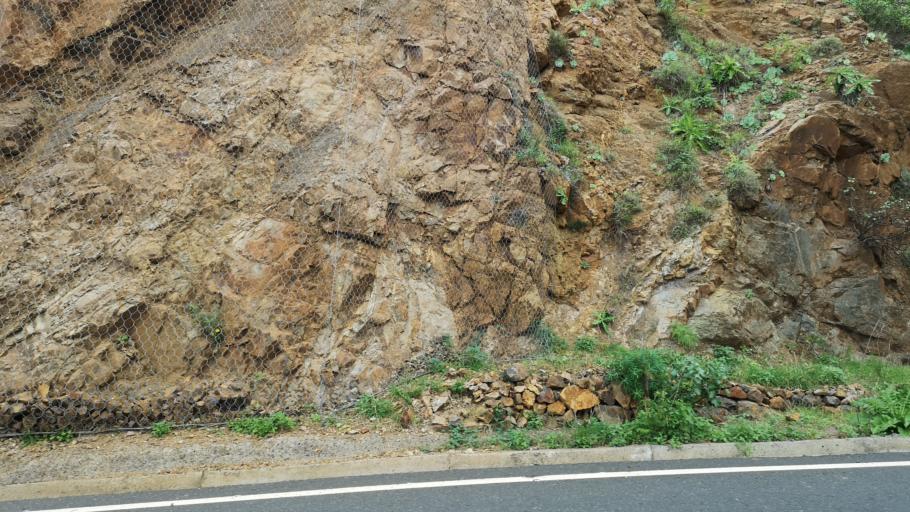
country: ES
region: Canary Islands
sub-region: Provincia de Santa Cruz de Tenerife
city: Agulo
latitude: 28.1907
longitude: -17.2022
